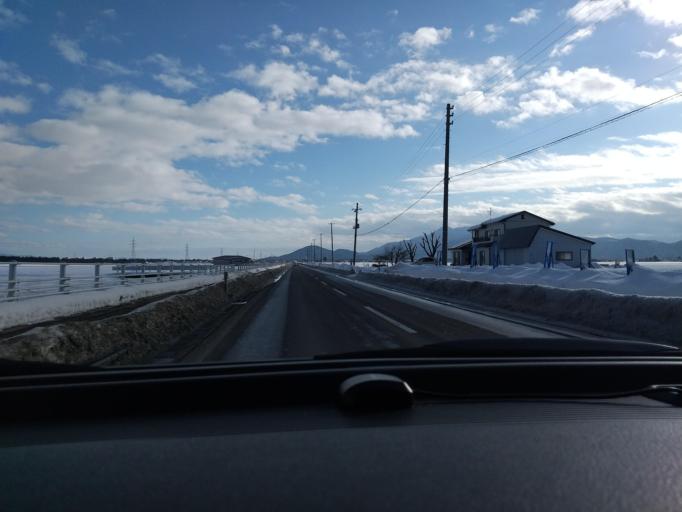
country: JP
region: Iwate
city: Morioka-shi
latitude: 39.7298
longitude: 141.0857
